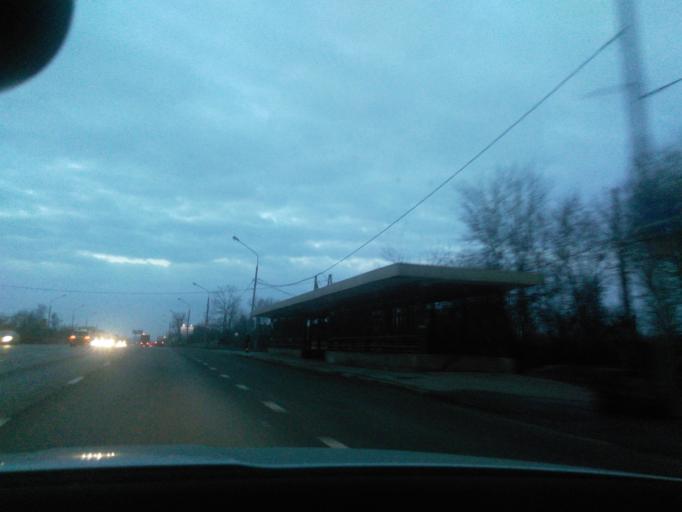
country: RU
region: Moskovskaya
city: Novopodrezkovo
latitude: 55.9261
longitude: 37.3849
